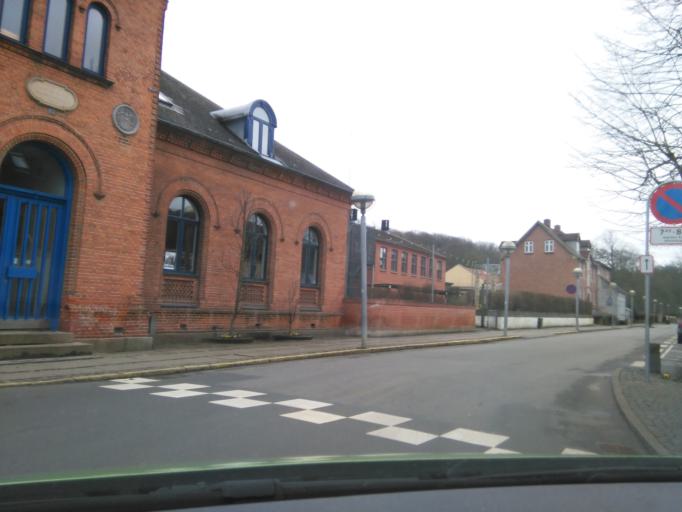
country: DK
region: Central Jutland
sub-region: Odder Kommune
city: Odder
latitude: 55.9705
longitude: 10.1398
